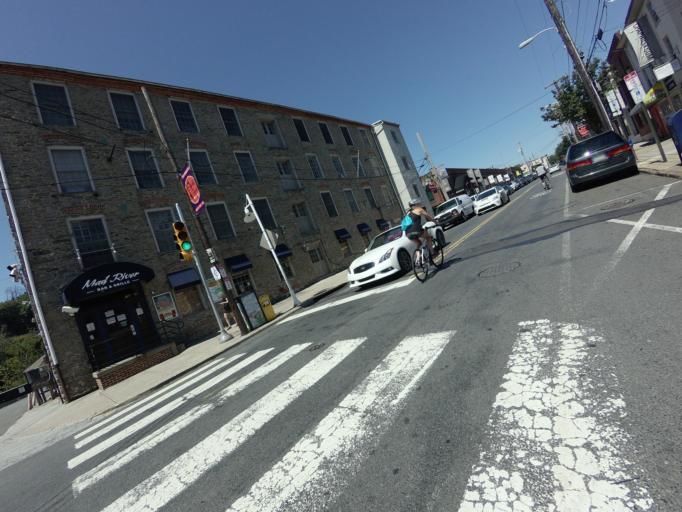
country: US
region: Pennsylvania
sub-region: Montgomery County
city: Bala-Cynwyd
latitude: 40.0222
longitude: -75.2183
